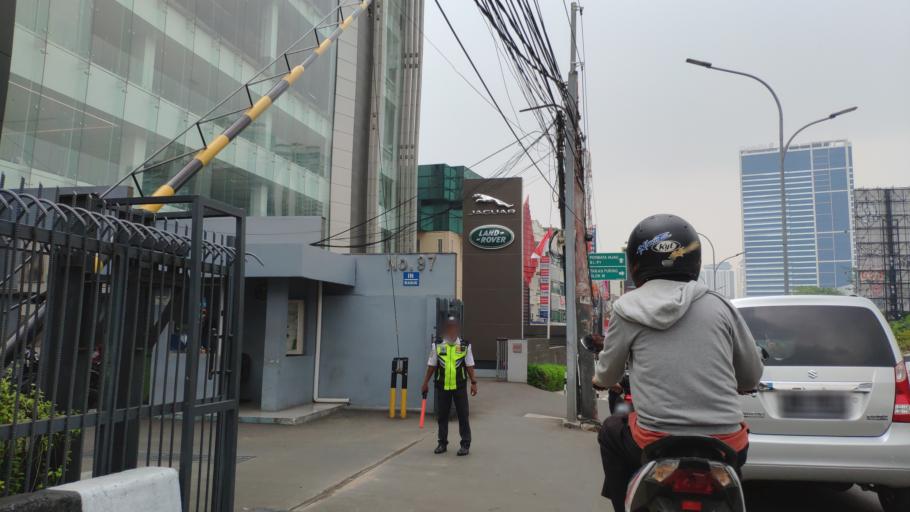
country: ID
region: Jakarta Raya
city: Jakarta
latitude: -6.2473
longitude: 106.7812
